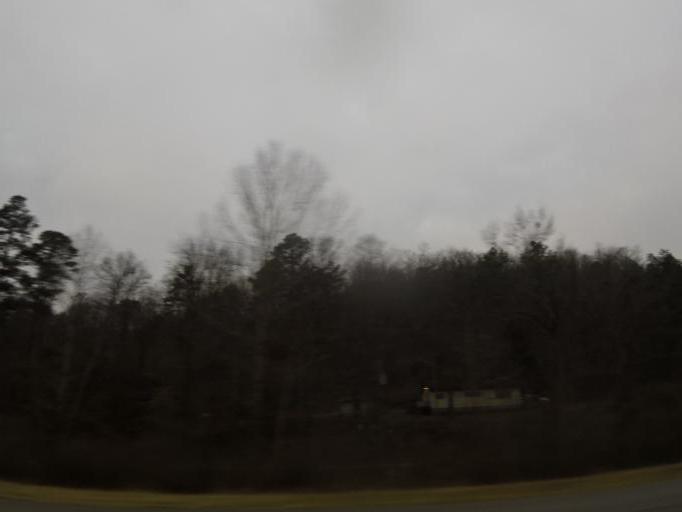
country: US
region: Alabama
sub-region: Cullman County
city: Good Hope
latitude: 34.0303
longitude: -86.8719
